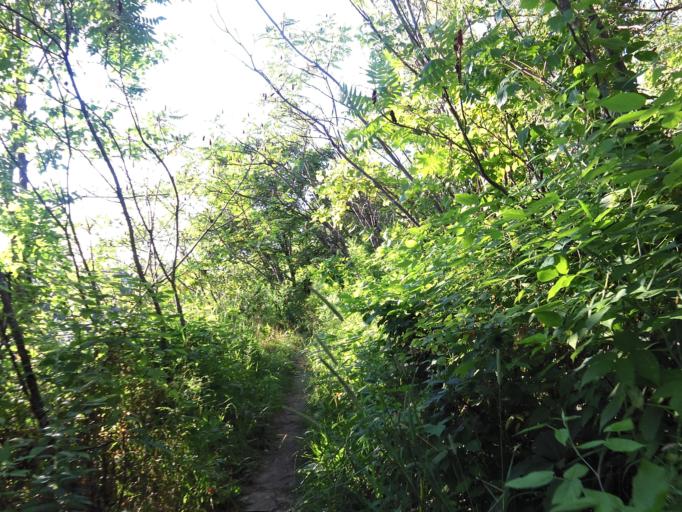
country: CA
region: Ontario
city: Ottawa
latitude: 45.3481
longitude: -75.6989
